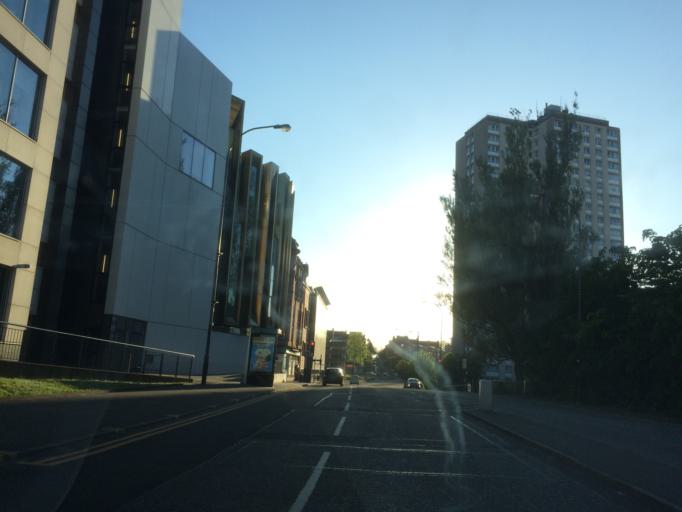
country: GB
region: Scotland
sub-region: Glasgow City
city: Glasgow
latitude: 55.8666
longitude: -4.2552
